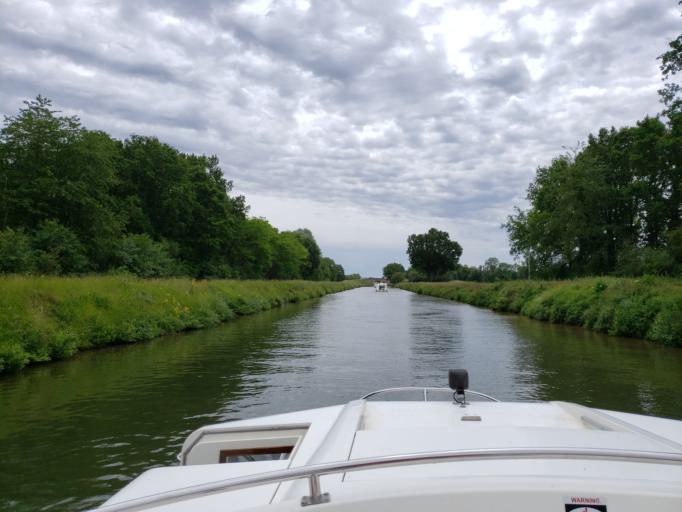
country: FR
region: Bourgogne
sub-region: Departement de l'Yonne
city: Appoigny
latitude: 47.8836
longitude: 3.5460
